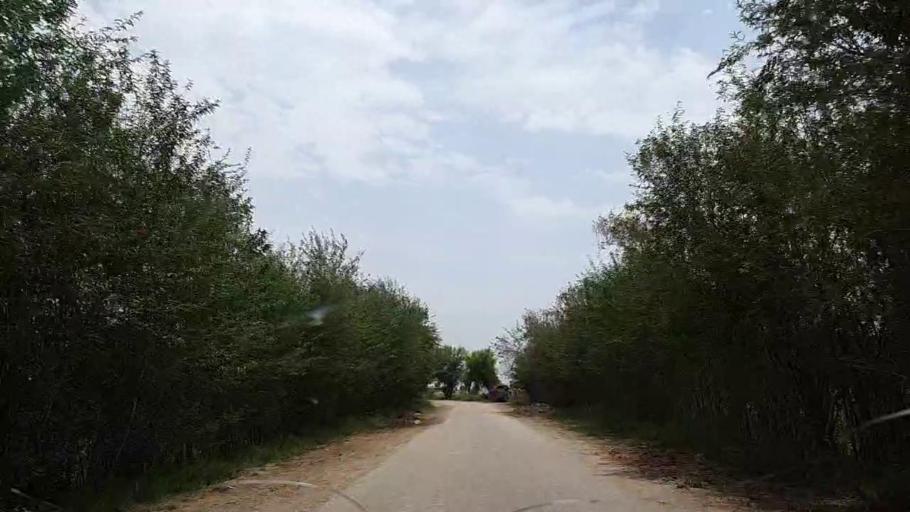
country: PK
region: Sindh
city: Tharu Shah
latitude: 26.9307
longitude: 68.1048
